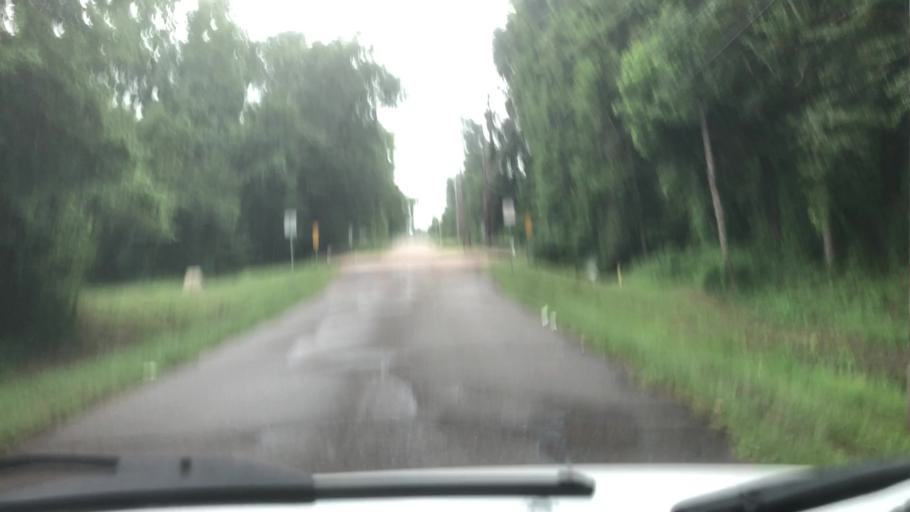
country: US
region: Texas
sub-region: Bowie County
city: Wake Village
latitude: 33.3964
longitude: -94.0844
